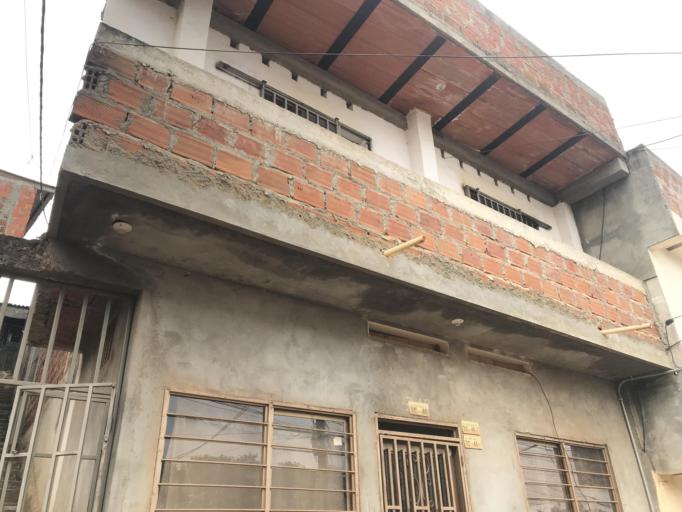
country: CO
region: Valle del Cauca
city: Cali
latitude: 3.3751
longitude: -76.5576
